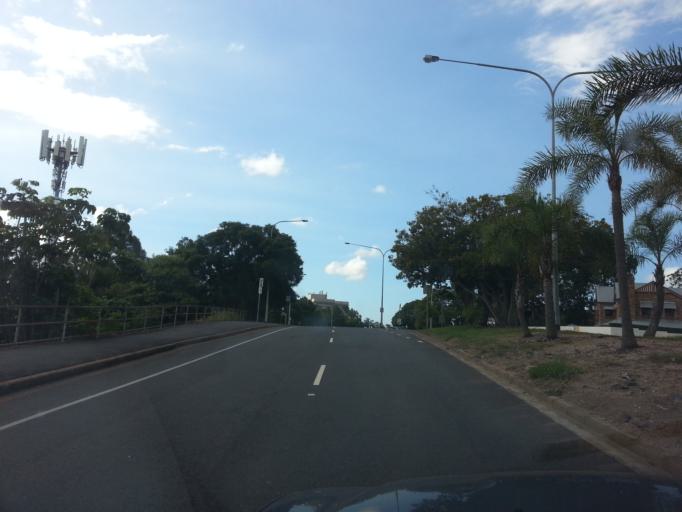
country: AU
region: Queensland
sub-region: Brisbane
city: Fortitude Valley
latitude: -27.4552
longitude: 153.0265
